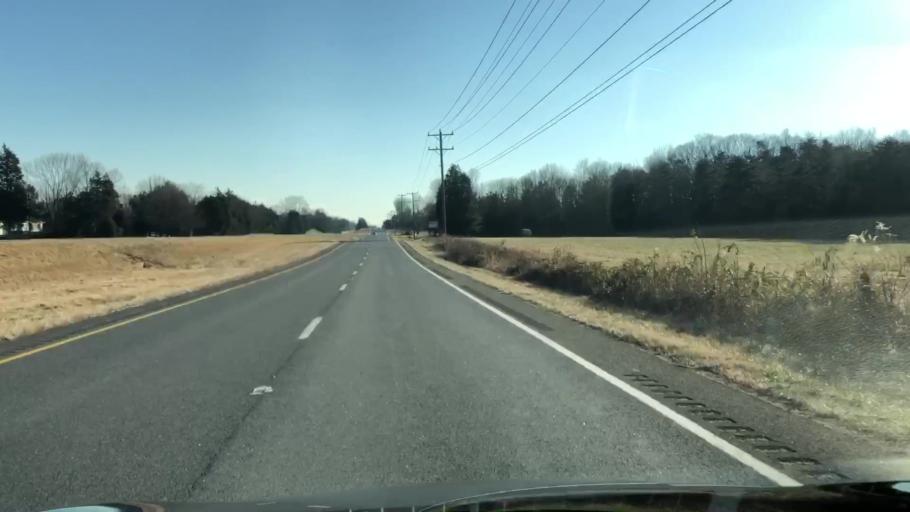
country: US
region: Virginia
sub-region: Fauquier County
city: Bealeton
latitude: 38.5749
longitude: -77.8019
